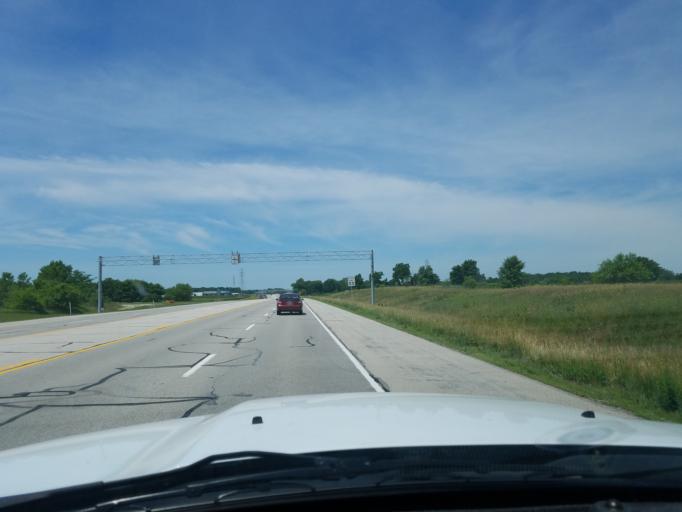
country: US
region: Indiana
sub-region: Delaware County
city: Daleville
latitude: 40.1137
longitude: -85.5207
